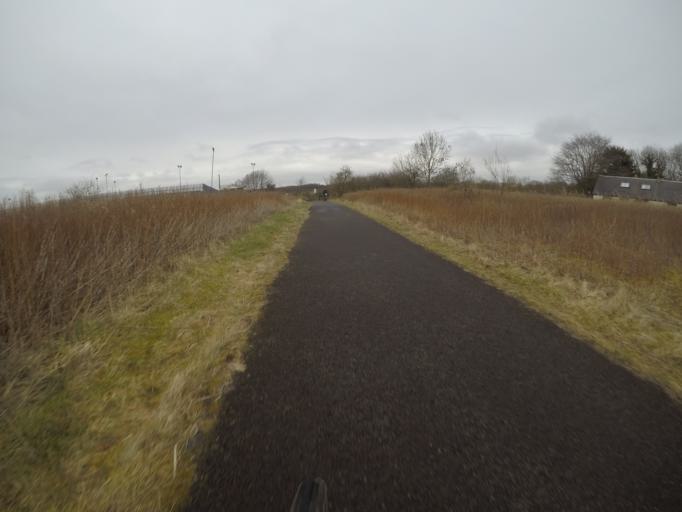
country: GB
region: Scotland
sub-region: North Ayrshire
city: Kilwinning
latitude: 55.6339
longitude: -4.6911
